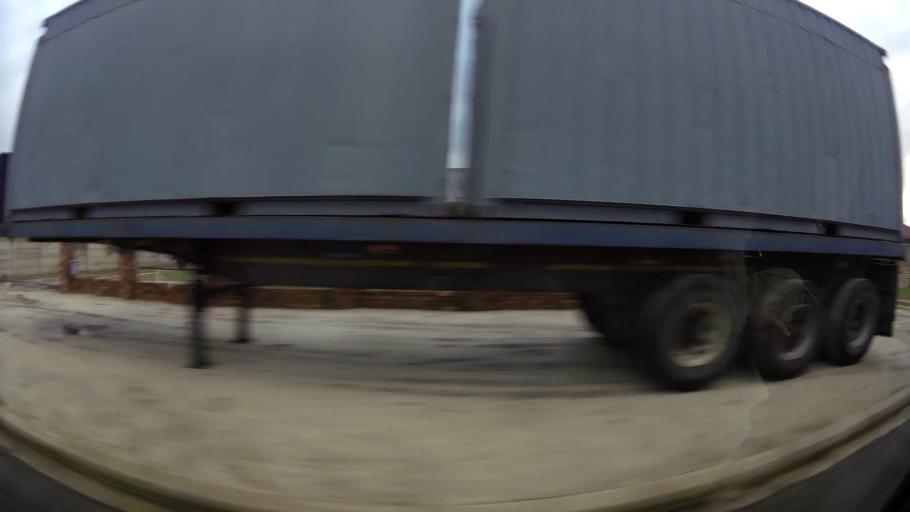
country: ZA
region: Eastern Cape
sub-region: Nelson Mandela Bay Metropolitan Municipality
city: Port Elizabeth
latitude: -33.9243
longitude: 25.6022
